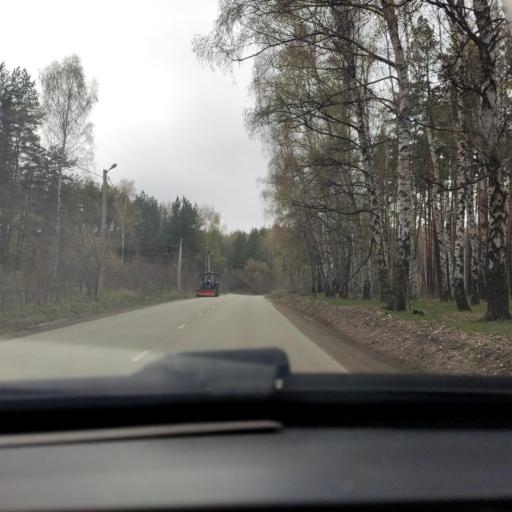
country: RU
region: Voronezj
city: Podgornoye
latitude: 51.7499
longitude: 39.1579
